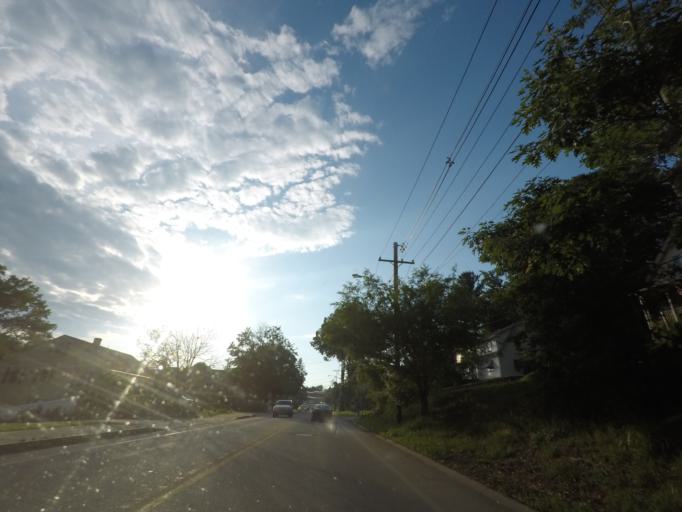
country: US
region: Massachusetts
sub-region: Worcester County
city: Southbridge
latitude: 42.0847
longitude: -72.0559
